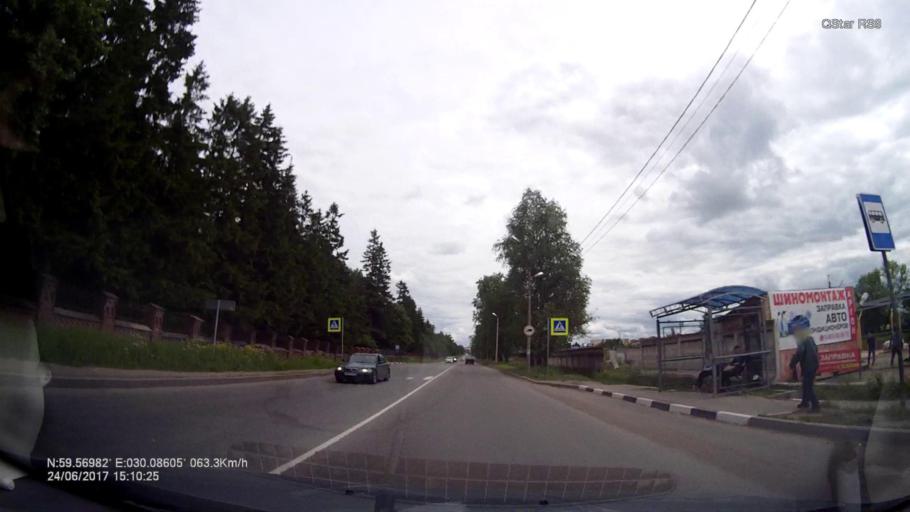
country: RU
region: Leningrad
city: Mariyenburg
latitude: 59.5697
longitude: 30.0862
